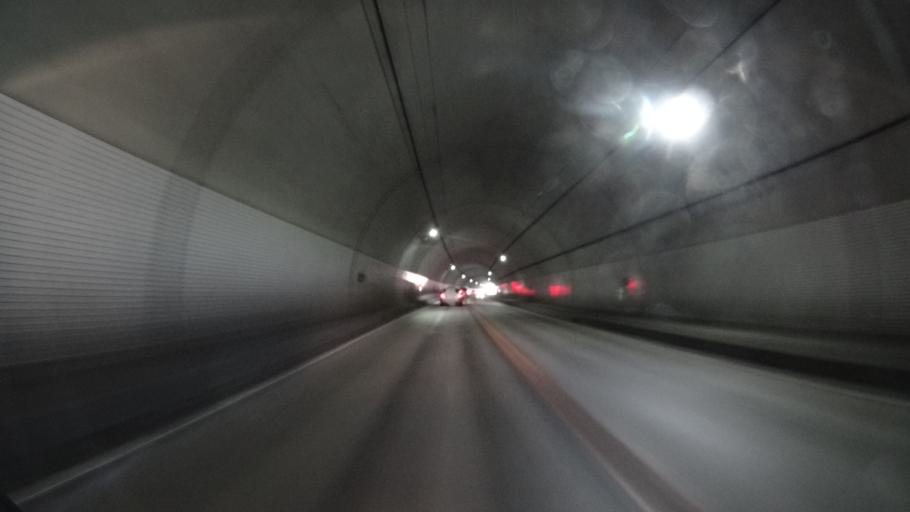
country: JP
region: Gunma
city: Numata
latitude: 36.6663
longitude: 139.1808
